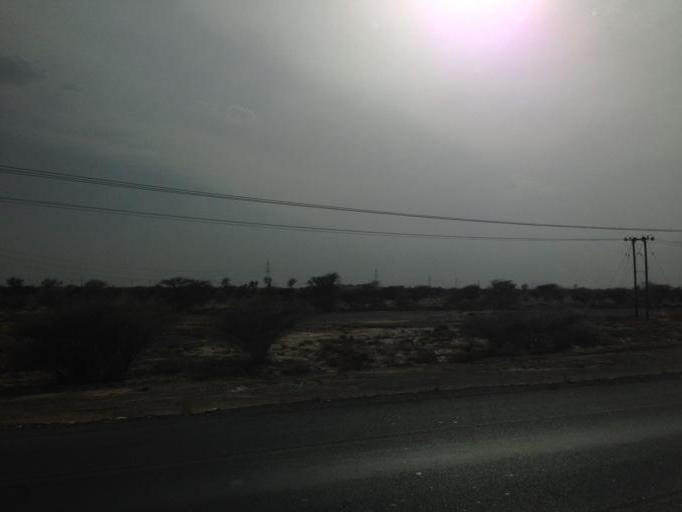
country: OM
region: Ash Sharqiyah
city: Al Qabil
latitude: 22.5998
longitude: 58.6710
